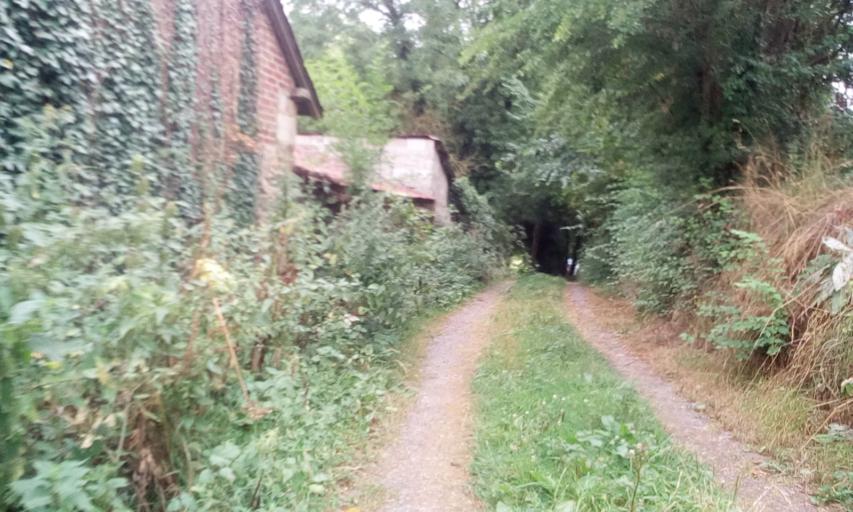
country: FR
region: Lower Normandy
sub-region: Departement du Calvados
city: Thury-Harcourt
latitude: 48.9947
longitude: -0.4243
